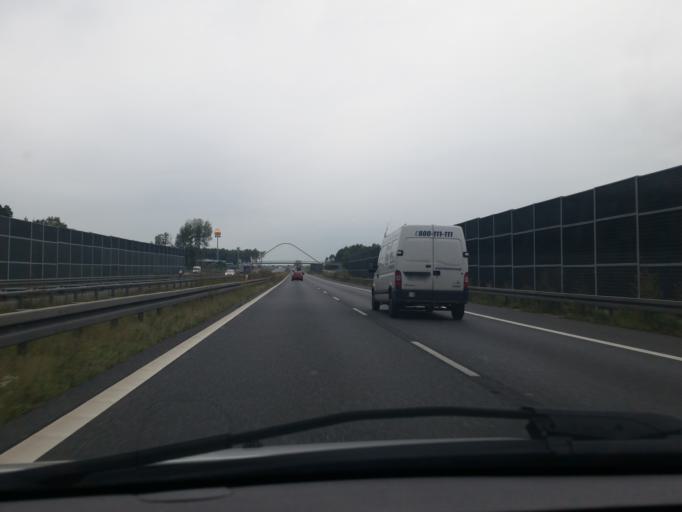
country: PL
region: Masovian Voivodeship
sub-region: Powiat zyrardowski
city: Mszczonow
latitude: 51.9563
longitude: 20.4954
